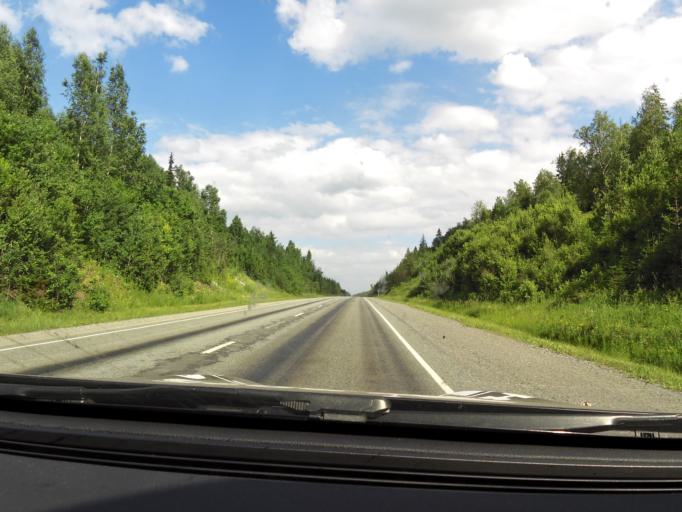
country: RU
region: Sverdlovsk
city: Bisert'
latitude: 56.8273
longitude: 59.2082
